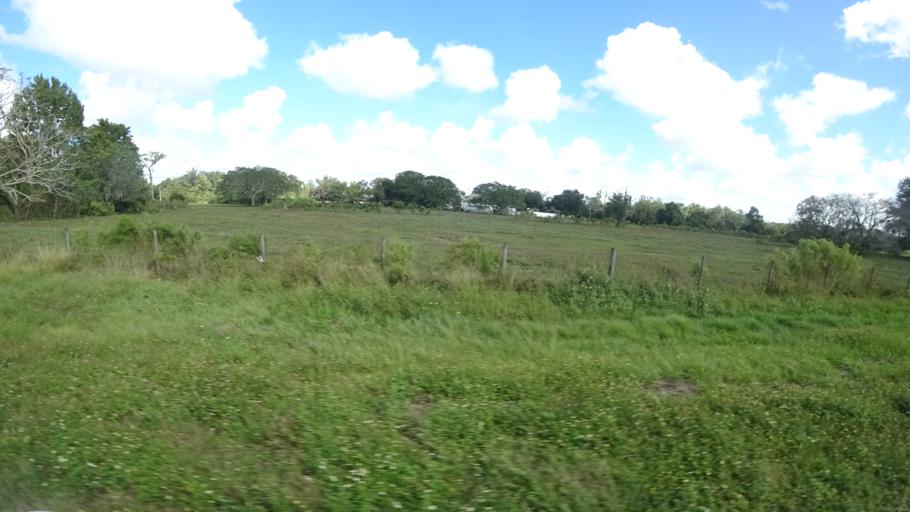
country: US
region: Florida
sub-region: Sarasota County
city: Lake Sarasota
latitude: 27.3454
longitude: -82.2348
